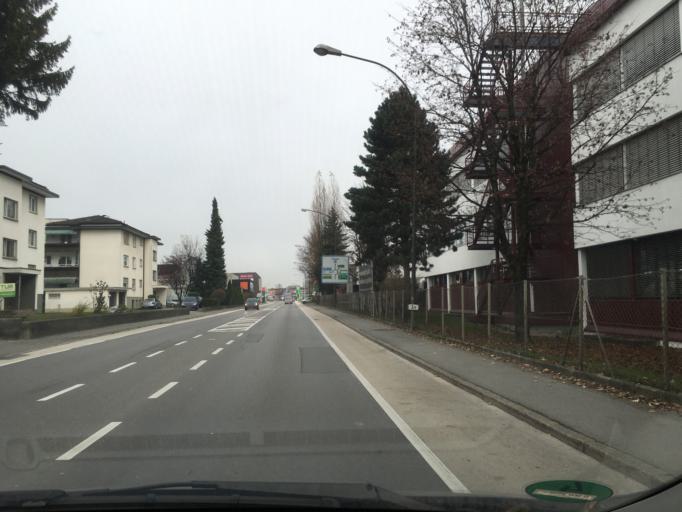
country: AT
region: Vorarlberg
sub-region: Politischer Bezirk Dornbirn
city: Hohenems
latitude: 47.3713
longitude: 9.6749
